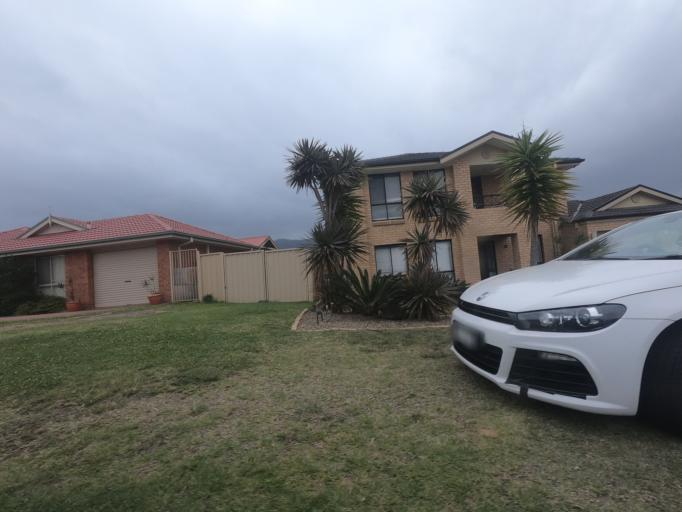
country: AU
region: New South Wales
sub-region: Wollongong
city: Dapto
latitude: -34.4838
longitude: 150.7776
